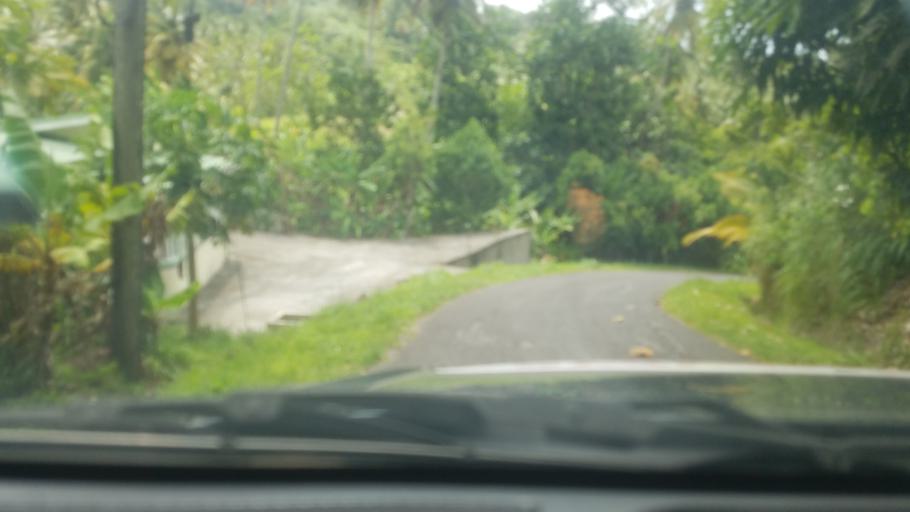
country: LC
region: Micoud Quarter
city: Micoud
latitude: 13.7987
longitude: -60.9463
